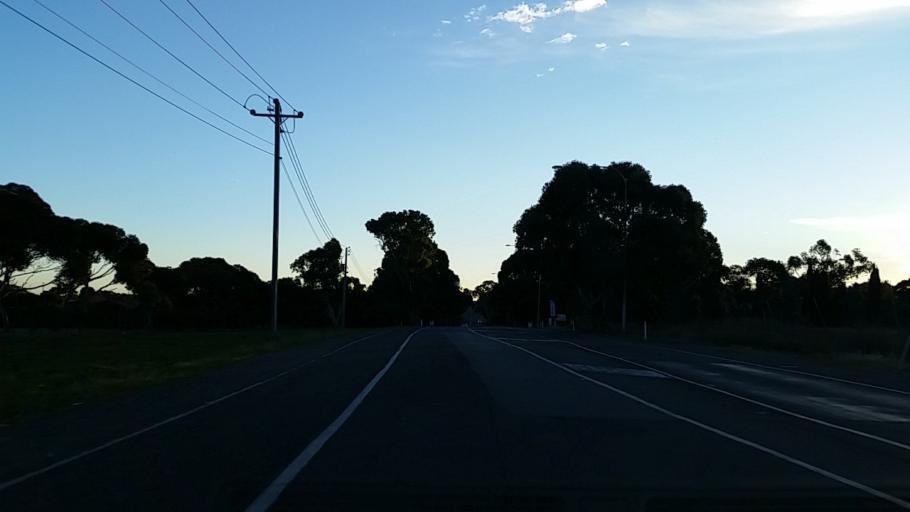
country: AU
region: South Australia
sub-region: Onkaparinga
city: Bedford Park
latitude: -35.0539
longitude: 138.5561
